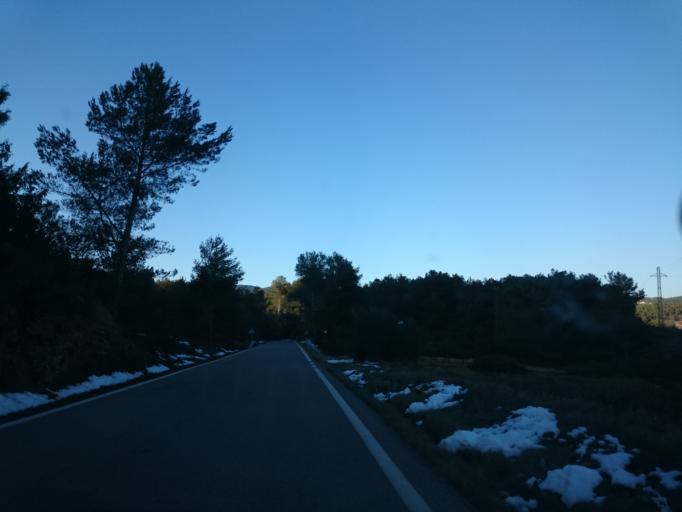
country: ES
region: Catalonia
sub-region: Provincia de Tarragona
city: la Bisbal del Penedes
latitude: 41.3620
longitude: 1.5025
